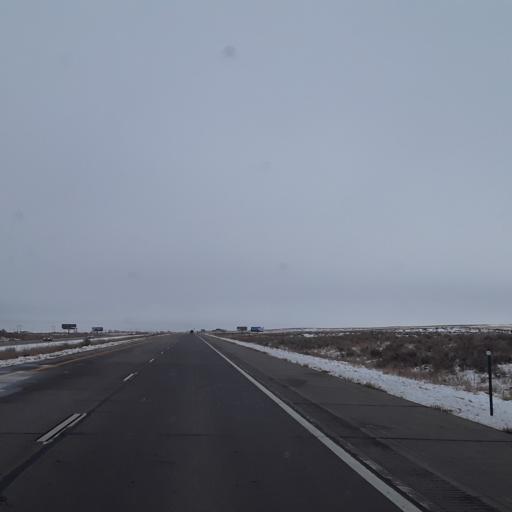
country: US
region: Colorado
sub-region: Logan County
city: Sterling
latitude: 40.5896
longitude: -103.1917
